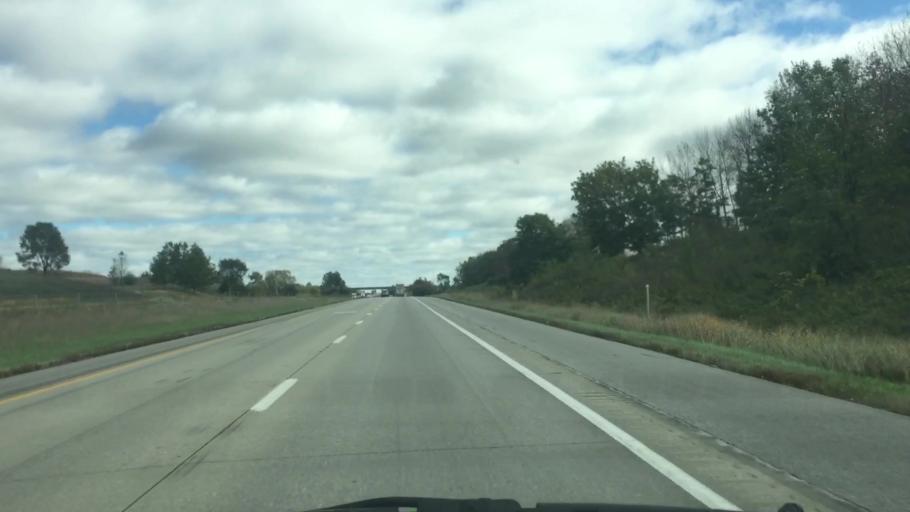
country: US
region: Iowa
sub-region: Jasper County
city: Newton
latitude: 41.6835
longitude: -93.0470
